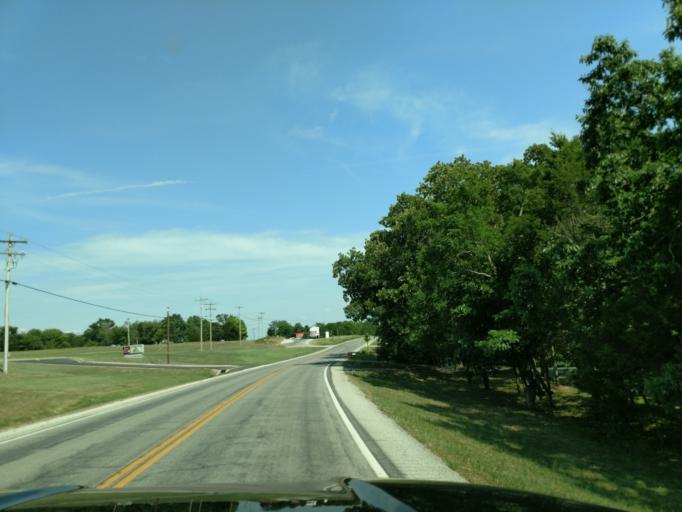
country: US
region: Missouri
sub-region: Barry County
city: Shell Knob
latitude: 36.6205
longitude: -93.6107
